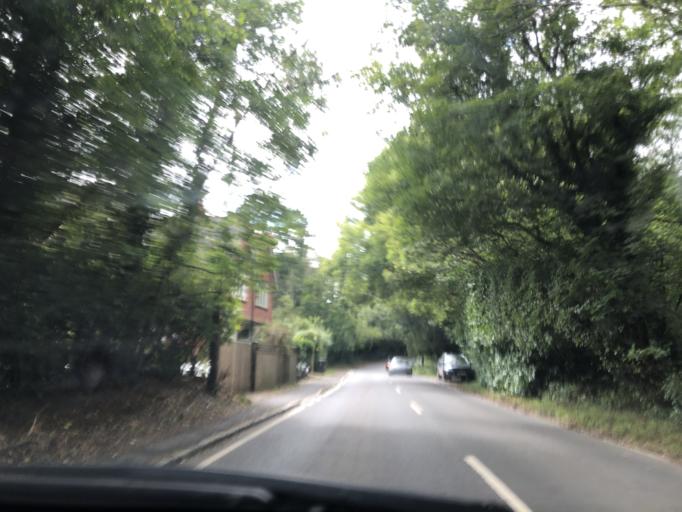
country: GB
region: England
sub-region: East Sussex
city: Forest Row
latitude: 51.0867
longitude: 0.0768
